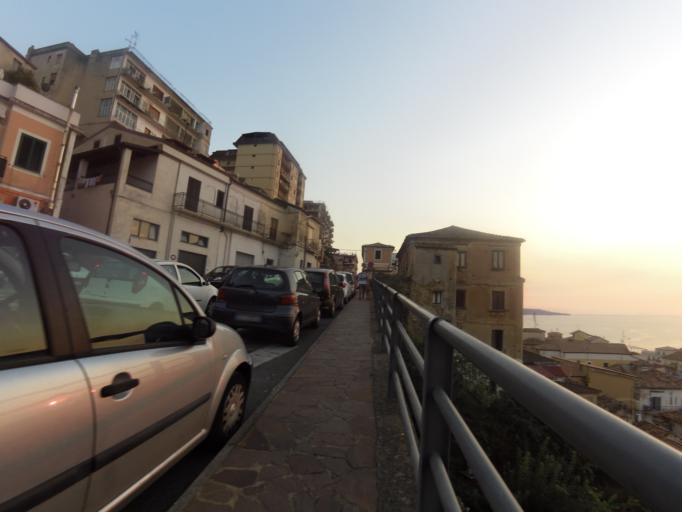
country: IT
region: Calabria
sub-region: Provincia di Vibo-Valentia
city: Maierato
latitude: 38.7354
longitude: 16.1639
